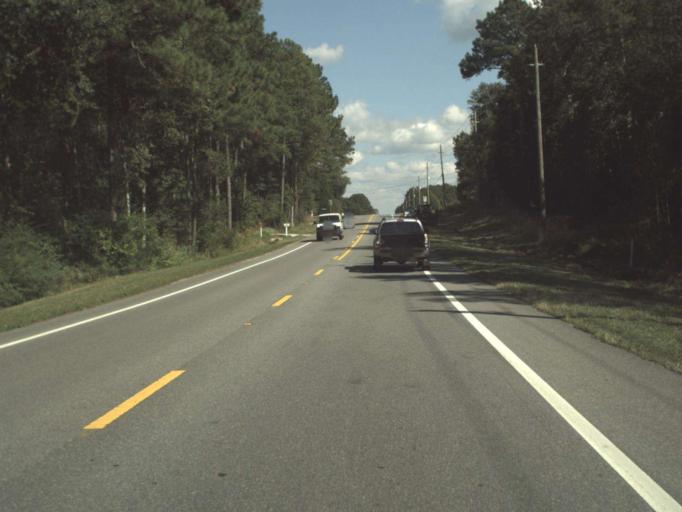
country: US
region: Florida
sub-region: Walton County
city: Freeport
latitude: 30.4789
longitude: -86.0731
